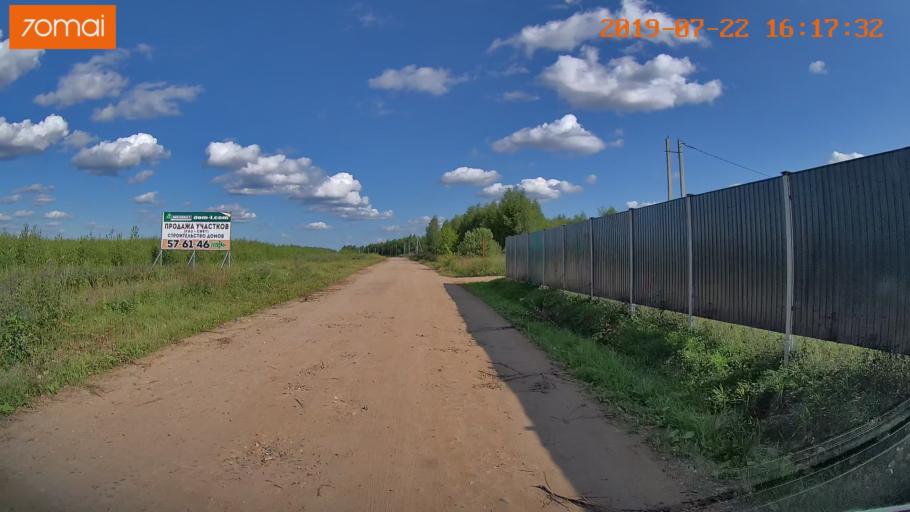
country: RU
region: Ivanovo
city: Novo-Talitsy
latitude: 57.0689
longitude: 40.8832
